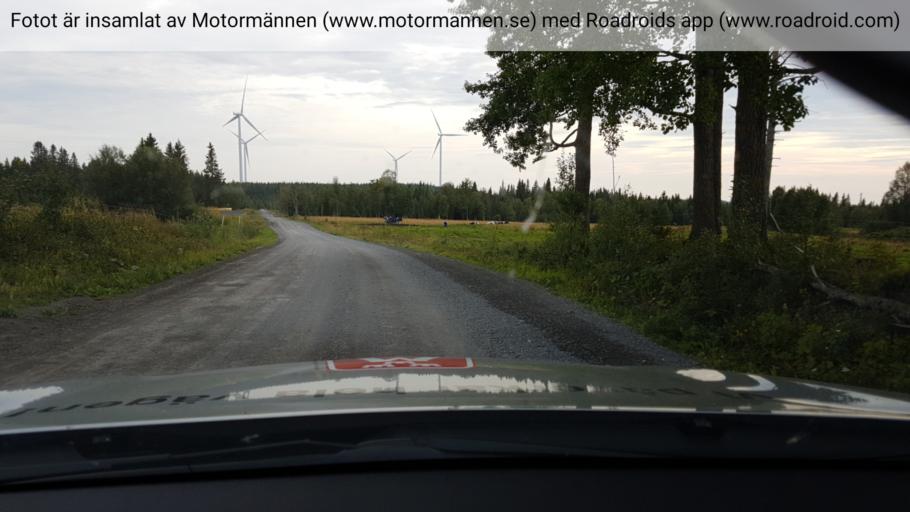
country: SE
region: Jaemtland
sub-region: OEstersunds Kommun
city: Lit
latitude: 63.6058
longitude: 14.9960
